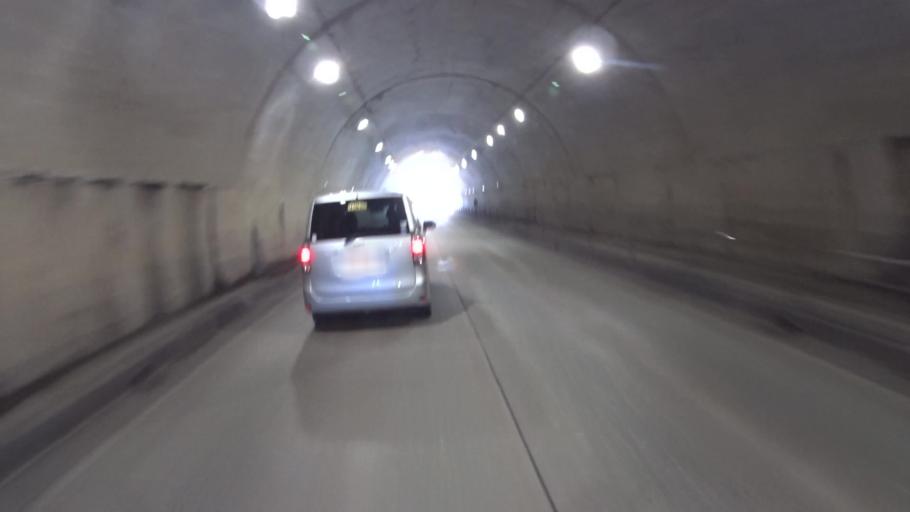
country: JP
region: Fukui
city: Obama
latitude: 35.4006
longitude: 135.6744
